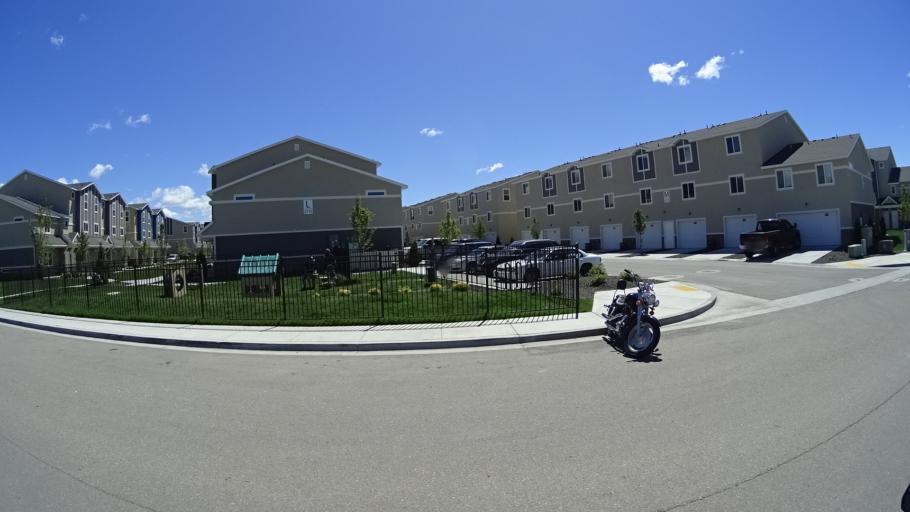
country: US
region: Idaho
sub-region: Ada County
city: Meridian
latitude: 43.6392
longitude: -116.3581
